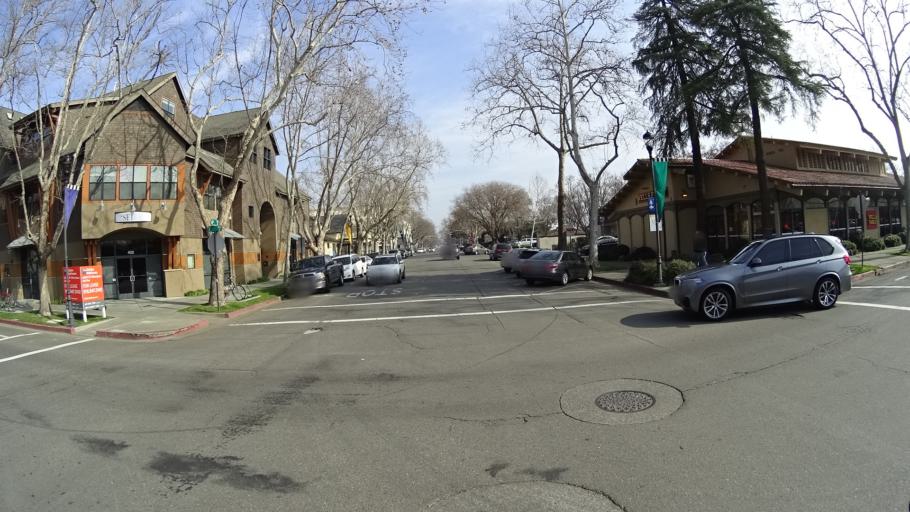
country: US
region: California
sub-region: Yolo County
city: Davis
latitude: 38.5460
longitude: -121.7408
